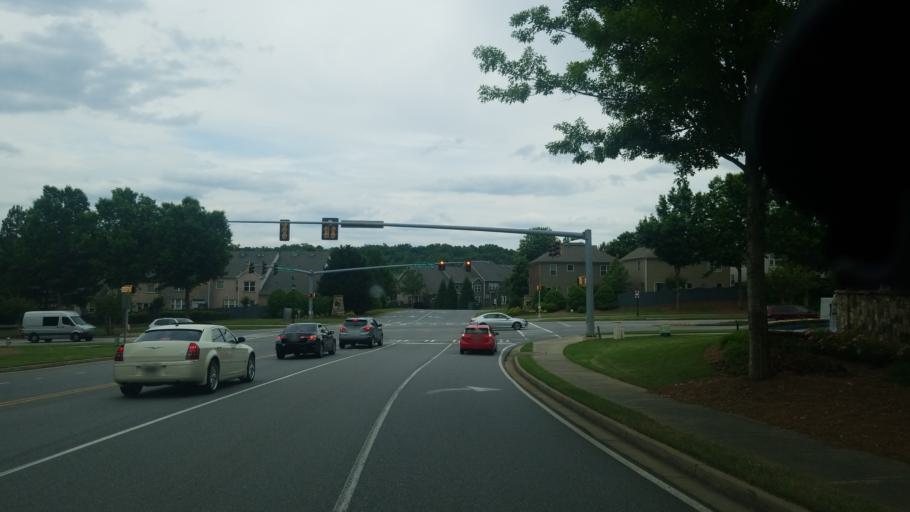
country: US
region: Georgia
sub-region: Forsyth County
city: Cumming
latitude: 34.1306
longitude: -84.1333
